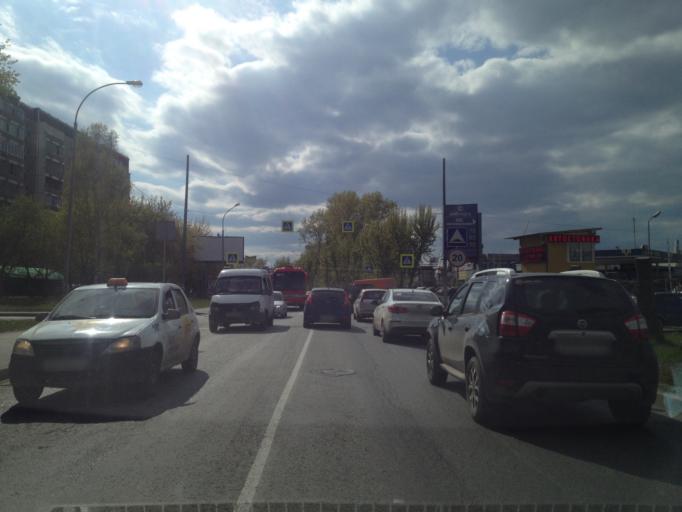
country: RU
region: Sverdlovsk
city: Yekaterinburg
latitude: 56.8574
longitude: 60.5580
